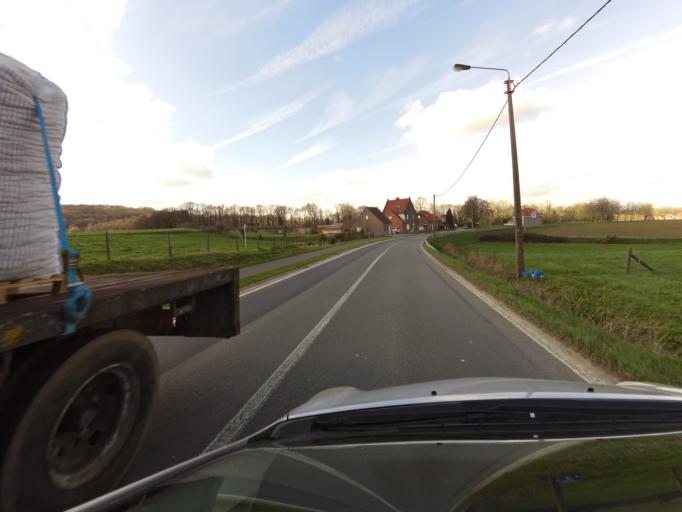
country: FR
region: Nord-Pas-de-Calais
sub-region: Departement du Nord
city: Nieppe
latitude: 50.7762
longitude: 2.8275
